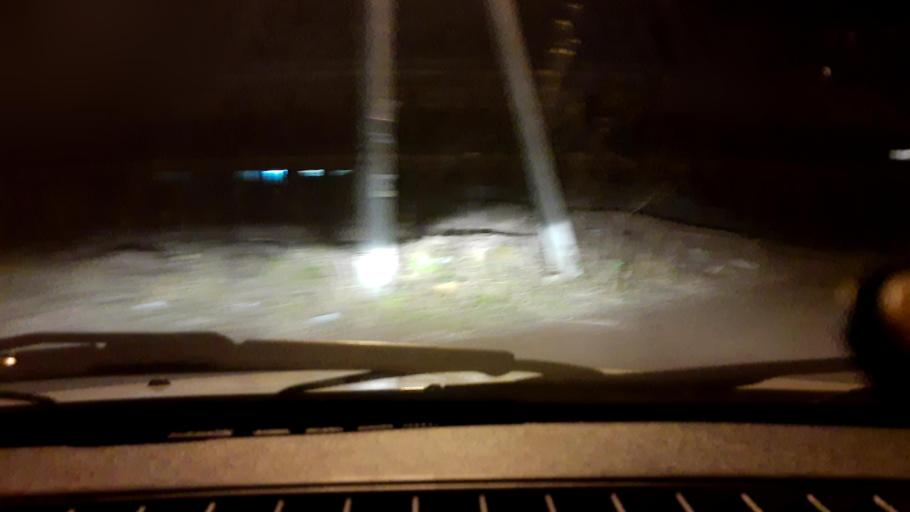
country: RU
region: Bashkortostan
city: Ufa
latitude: 54.6796
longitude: 55.9772
